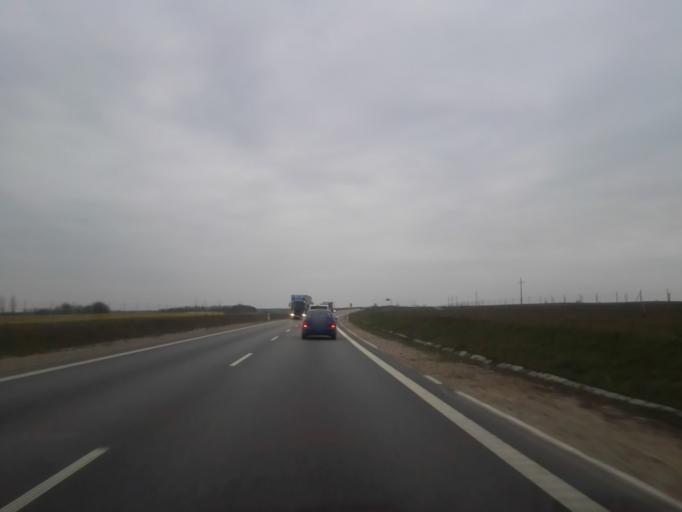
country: PL
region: Podlasie
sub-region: Powiat kolnenski
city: Stawiski
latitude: 53.3988
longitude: 22.1557
